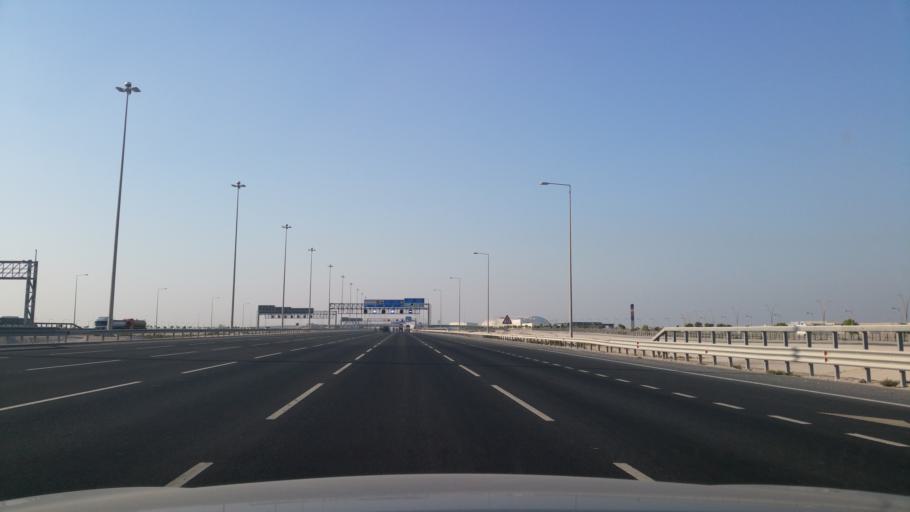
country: QA
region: Al Wakrah
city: Al Wakrah
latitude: 25.1398
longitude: 51.5823
